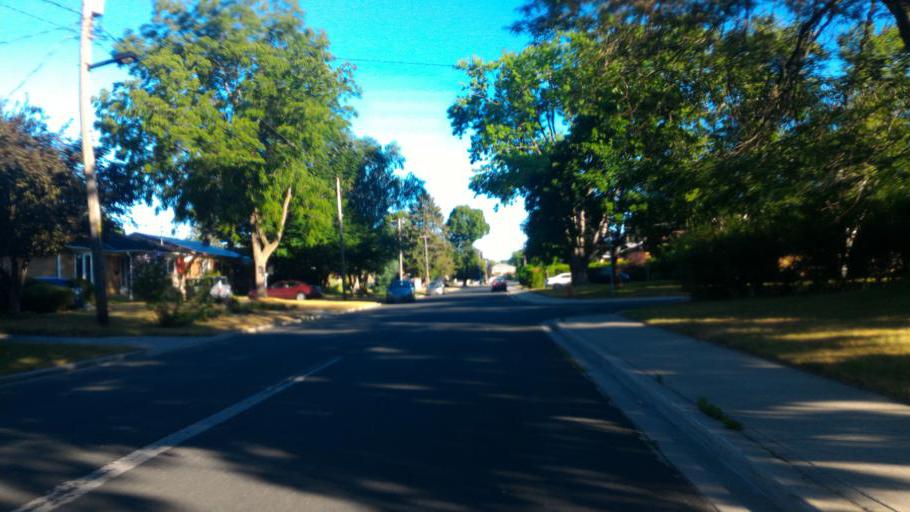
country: CA
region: Ontario
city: Burlington
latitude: 43.3401
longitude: -79.7985
